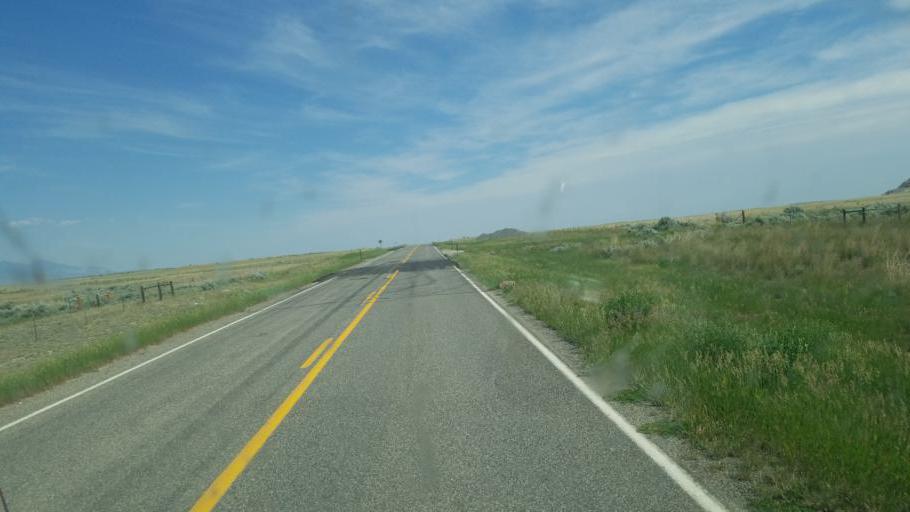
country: US
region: Wyoming
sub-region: Park County
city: Powell
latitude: 44.7815
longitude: -108.9338
